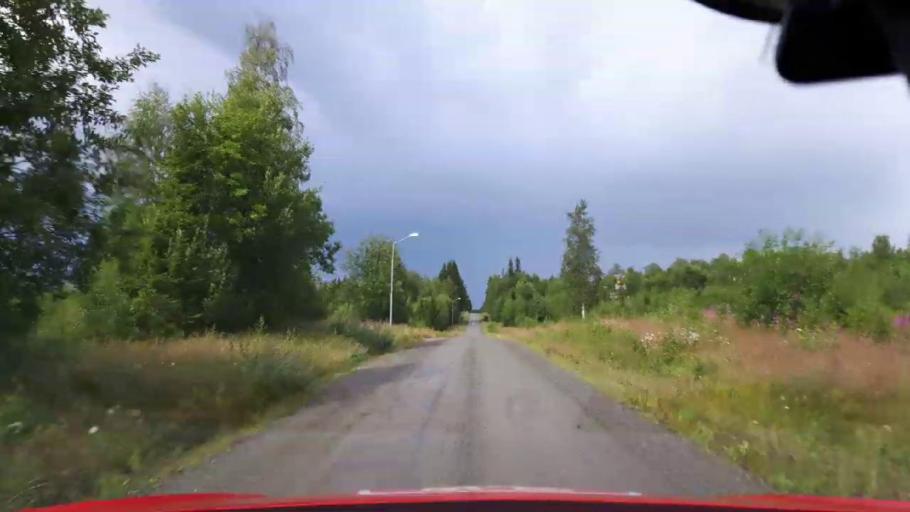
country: SE
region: Jaemtland
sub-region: Stroemsunds Kommun
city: Stroemsund
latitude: 64.0601
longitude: 15.8900
